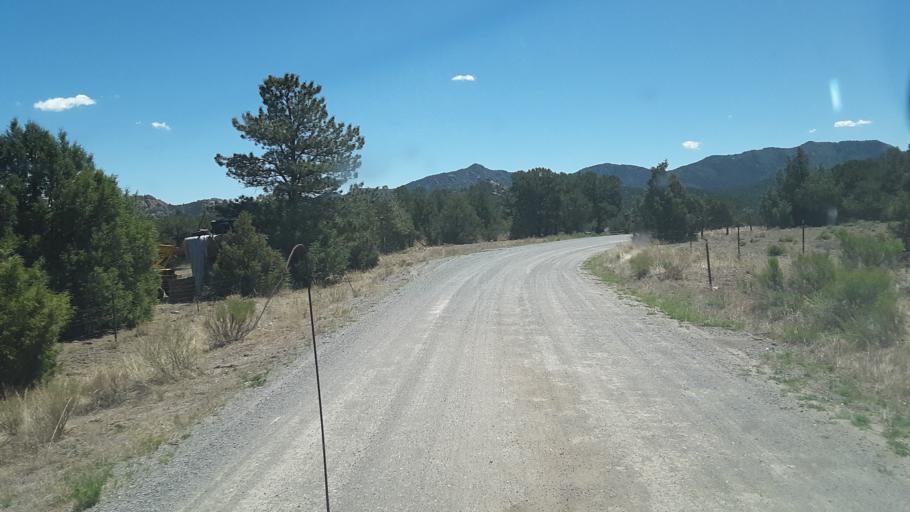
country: US
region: Colorado
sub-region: Custer County
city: Westcliffe
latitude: 38.3055
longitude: -105.6168
